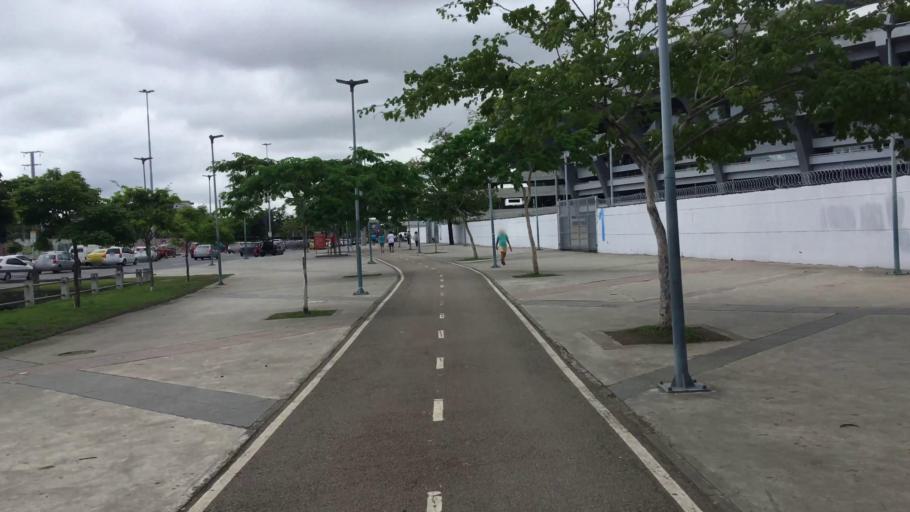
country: BR
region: Rio de Janeiro
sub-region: Rio De Janeiro
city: Rio de Janeiro
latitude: -22.9106
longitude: -43.2321
